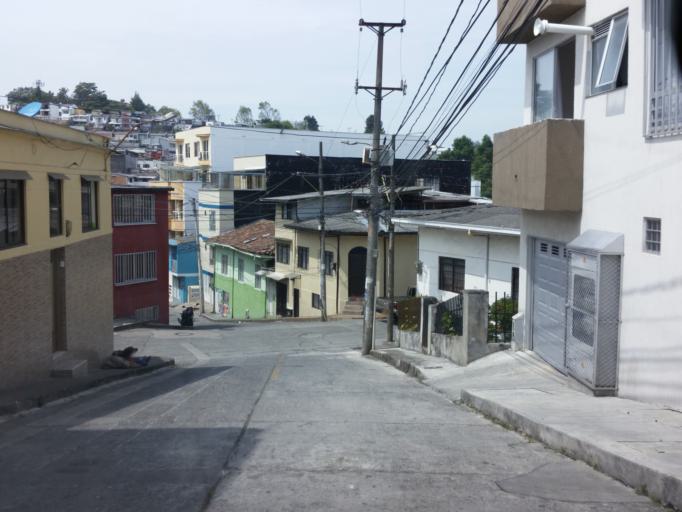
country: CO
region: Caldas
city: Manizales
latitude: 5.0783
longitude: -75.5243
